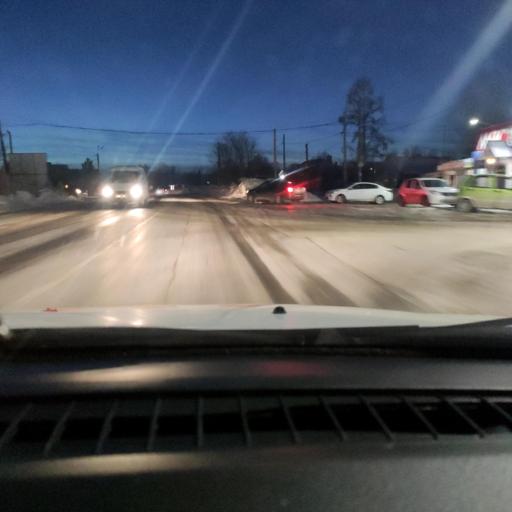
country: RU
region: Samara
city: Kinel'
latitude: 53.2694
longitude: 50.5808
